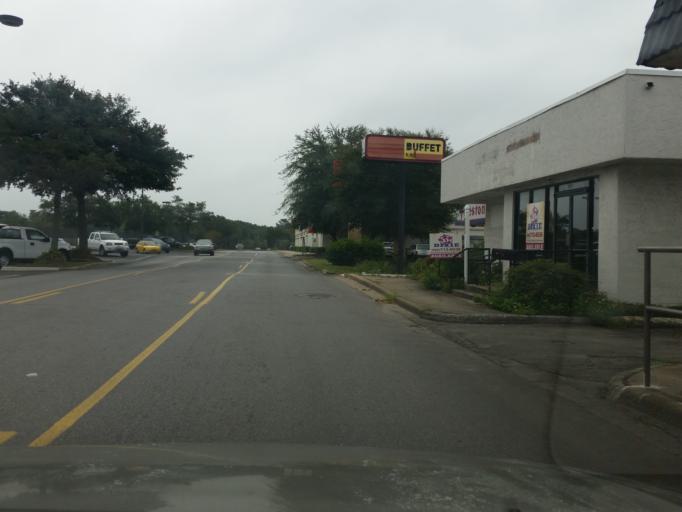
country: US
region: Florida
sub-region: Escambia County
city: Brent
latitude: 30.4735
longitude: -87.2096
